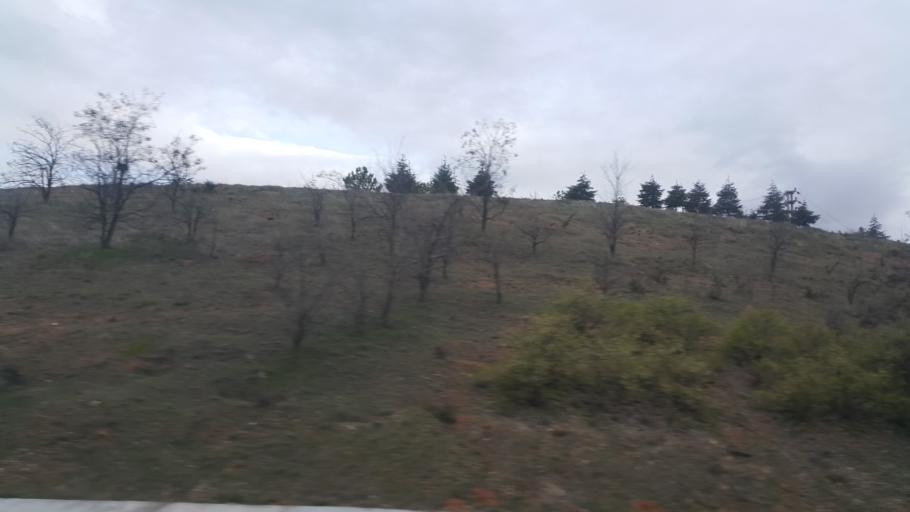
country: TR
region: Ankara
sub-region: Goelbasi
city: Golbasi
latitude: 39.8065
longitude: 32.7963
